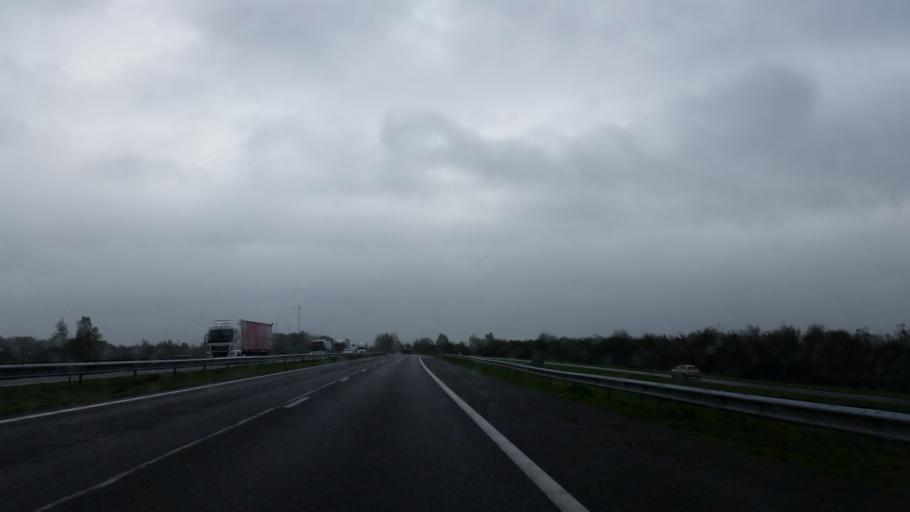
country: NL
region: Friesland
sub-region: Gemeente Boarnsterhim
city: Grou
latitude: 53.0900
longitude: 5.8236
